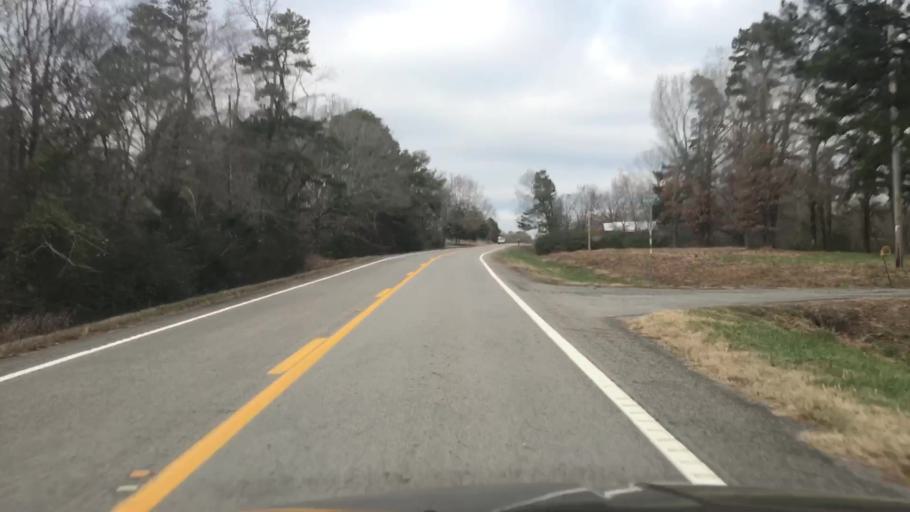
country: US
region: Arkansas
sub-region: Montgomery County
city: Mount Ida
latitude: 34.6513
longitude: -93.7541
